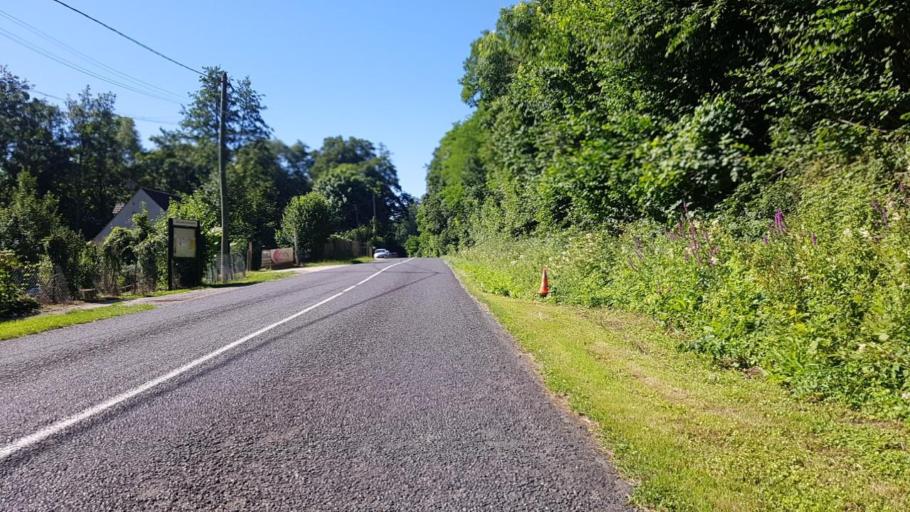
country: FR
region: Picardie
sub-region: Departement de l'Aisne
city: Chezy-sur-Marne
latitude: 48.9926
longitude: 3.3427
